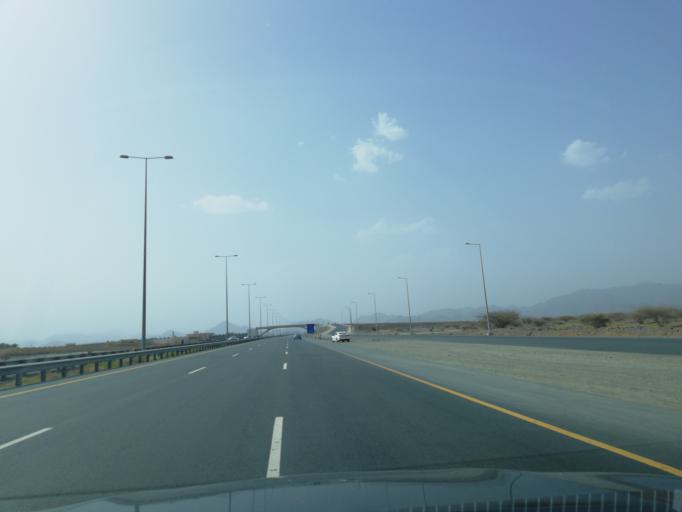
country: OM
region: Muhafazat ad Dakhiliyah
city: Sufalat Sama'il
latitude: 23.0366
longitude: 58.2023
